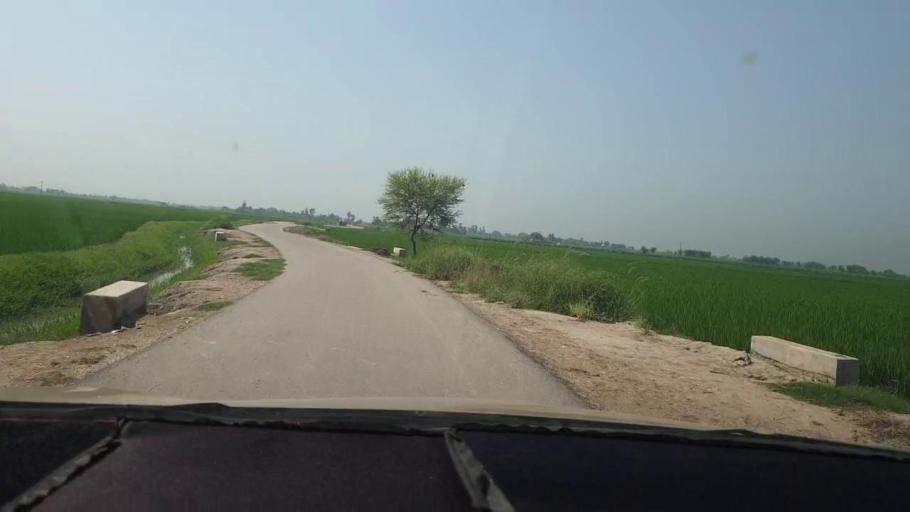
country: PK
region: Sindh
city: Kambar
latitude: 27.5665
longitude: 68.0445
